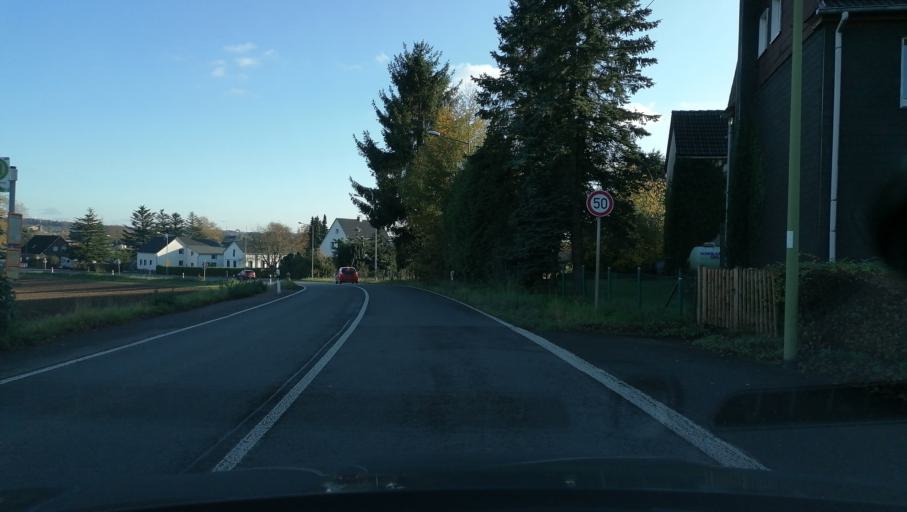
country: DE
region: North Rhine-Westphalia
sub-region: Regierungsbezirk Arnsberg
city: Schwelm
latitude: 51.2647
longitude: 7.3249
